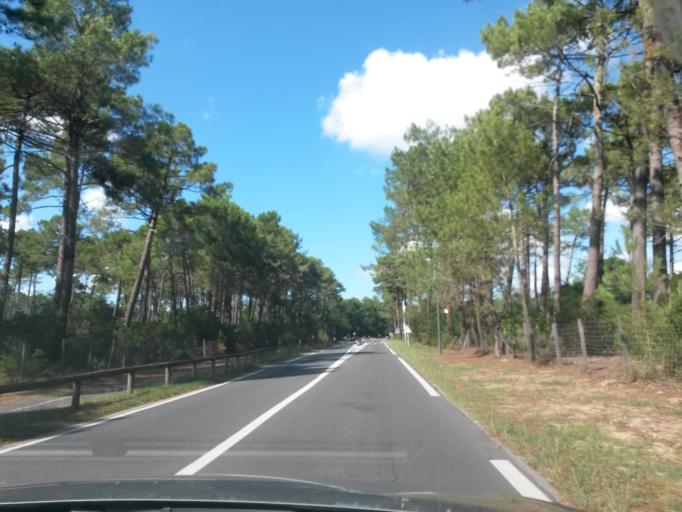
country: FR
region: Aquitaine
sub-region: Departement de la Gironde
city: Ares
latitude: 44.7331
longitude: -1.1963
